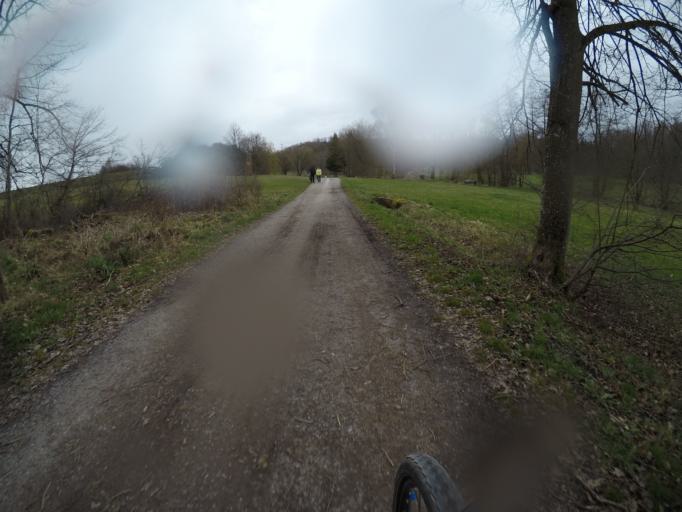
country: DE
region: Baden-Wuerttemberg
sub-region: Regierungsbezirk Stuttgart
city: Ehningen
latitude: 48.6545
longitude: 8.9662
